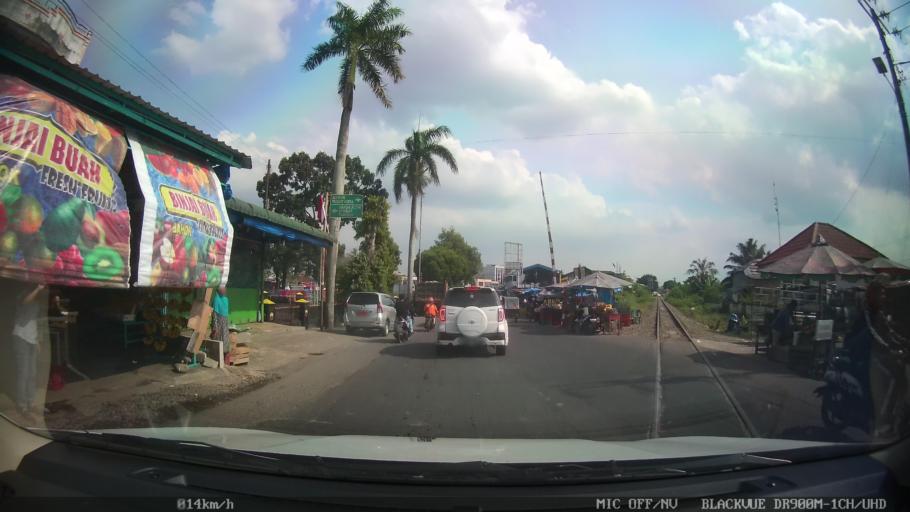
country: ID
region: North Sumatra
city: Binjai
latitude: 3.6173
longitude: 98.4969
